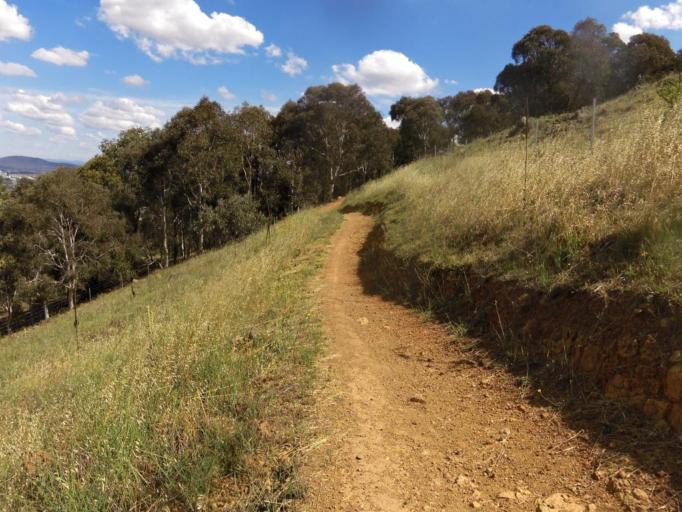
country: AU
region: Australian Capital Territory
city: Belconnen
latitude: -35.1447
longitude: 149.0921
